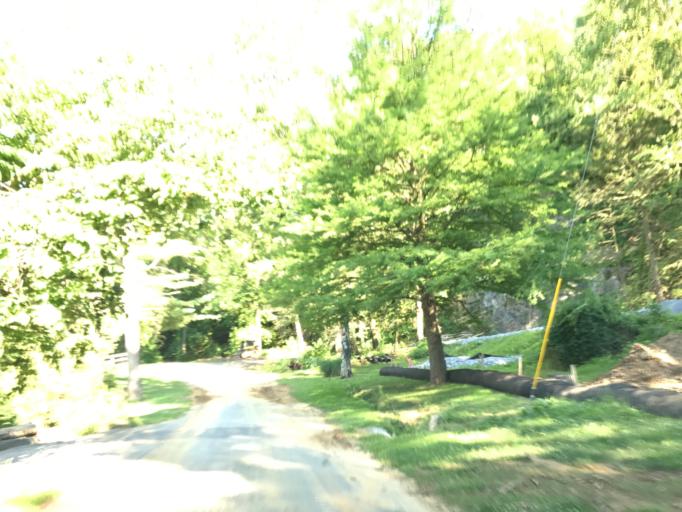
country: US
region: Pennsylvania
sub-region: Lancaster County
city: Conestoga
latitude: 39.9234
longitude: -76.3273
